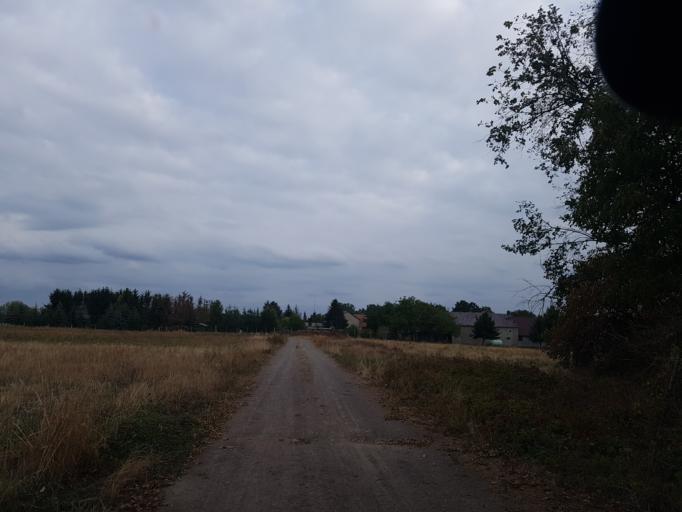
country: DE
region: Brandenburg
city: Schilda
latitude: 51.6331
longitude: 13.3181
